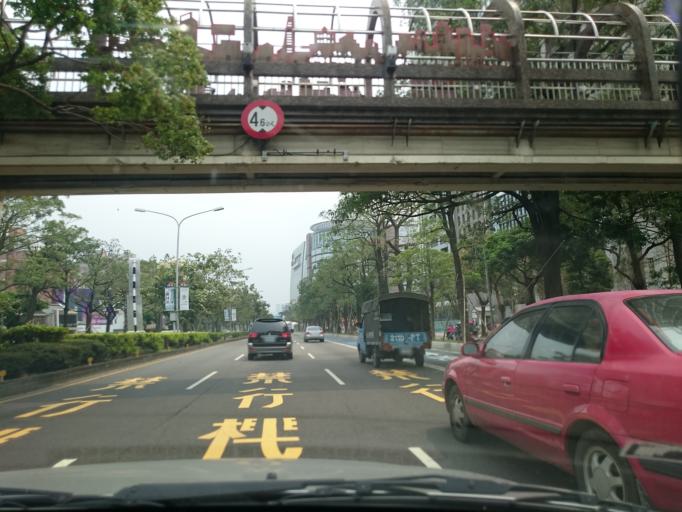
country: TW
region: Taiwan
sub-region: Taichung City
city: Taichung
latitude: 24.1676
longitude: 120.6412
